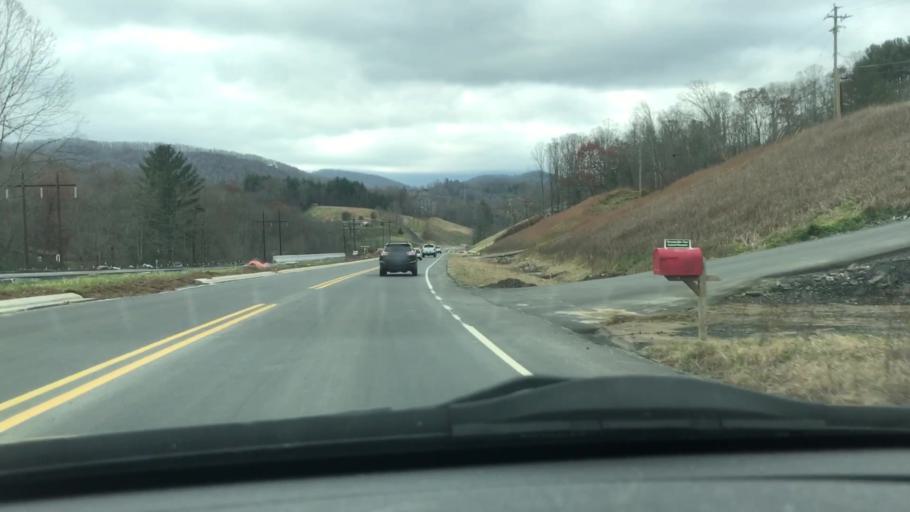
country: US
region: North Carolina
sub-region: Mitchell County
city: Spruce Pine
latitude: 35.9046
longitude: -82.1075
